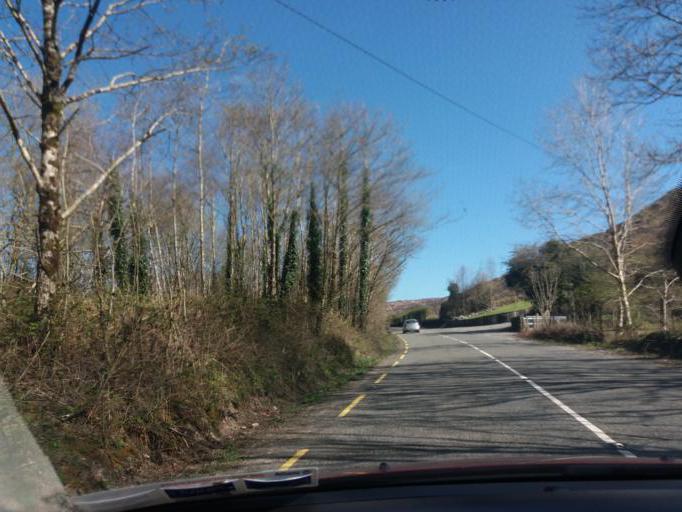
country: IE
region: Munster
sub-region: Ciarrai
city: Cill Airne
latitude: 51.9261
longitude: -9.3843
